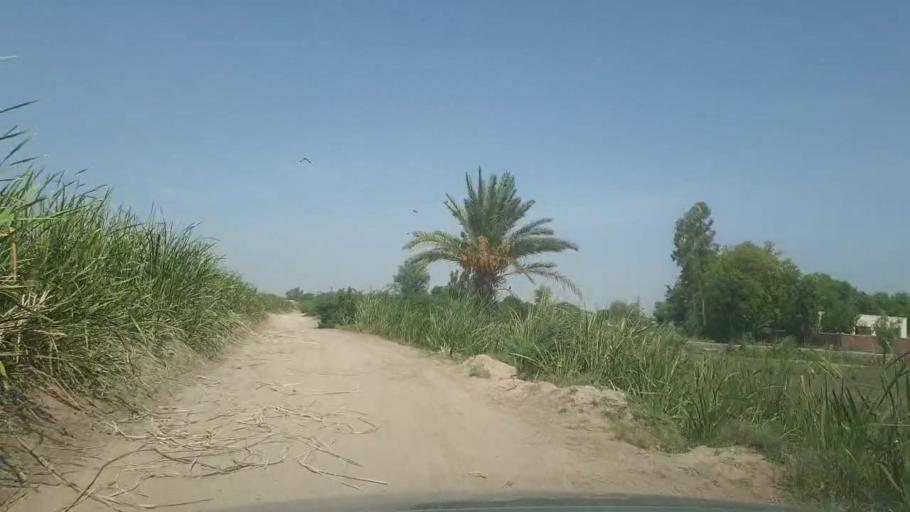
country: PK
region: Sindh
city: Khairpur
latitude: 27.3999
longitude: 69.0447
